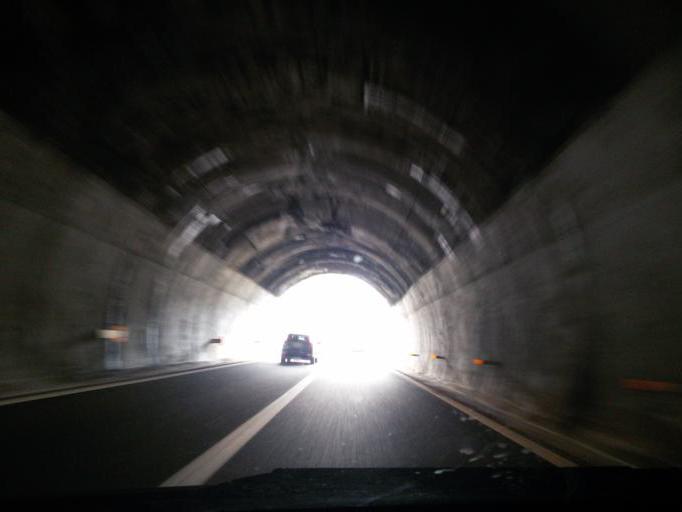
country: IT
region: Liguria
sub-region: Provincia di Genova
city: Genoa
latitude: 44.4456
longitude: 8.9075
